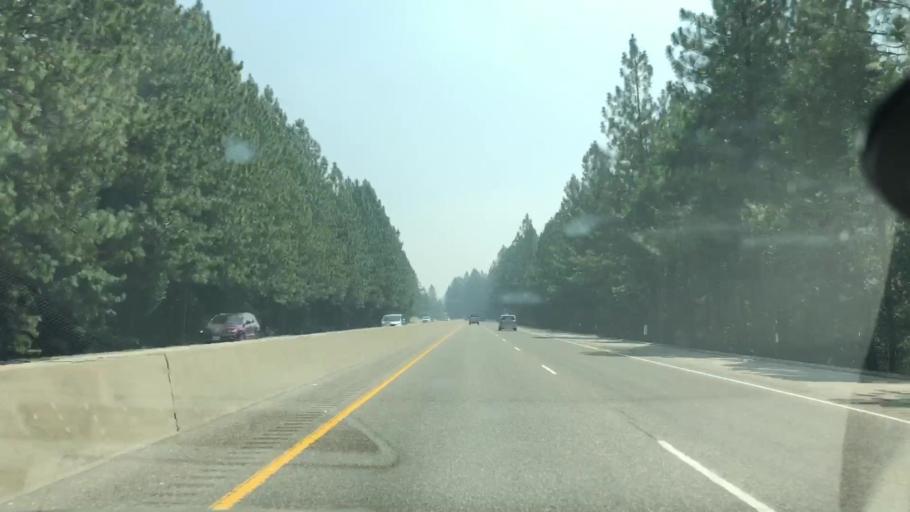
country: US
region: California
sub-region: El Dorado County
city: Camino
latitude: 38.7439
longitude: -120.6542
